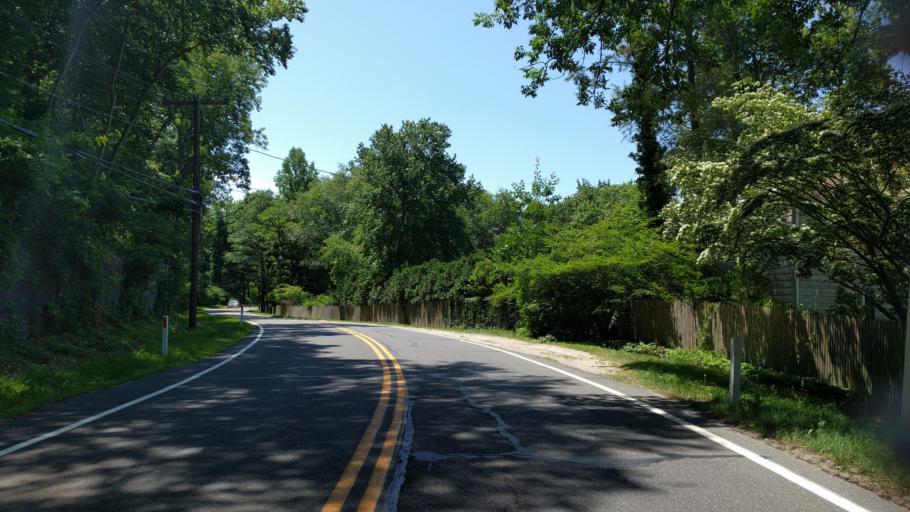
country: US
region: New York
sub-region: Nassau County
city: Oyster Bay
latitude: 40.8664
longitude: -73.5417
